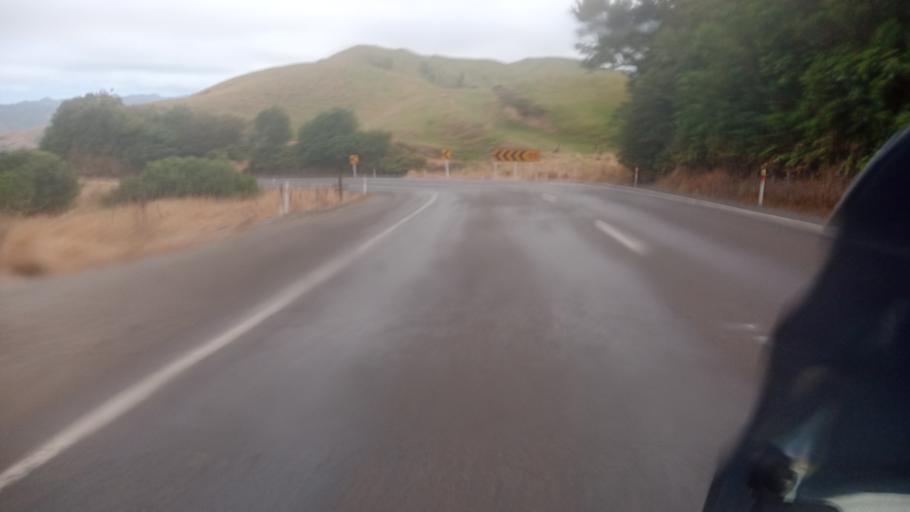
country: NZ
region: Bay of Plenty
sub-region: Opotiki District
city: Opotiki
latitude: -38.3584
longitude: 177.4532
